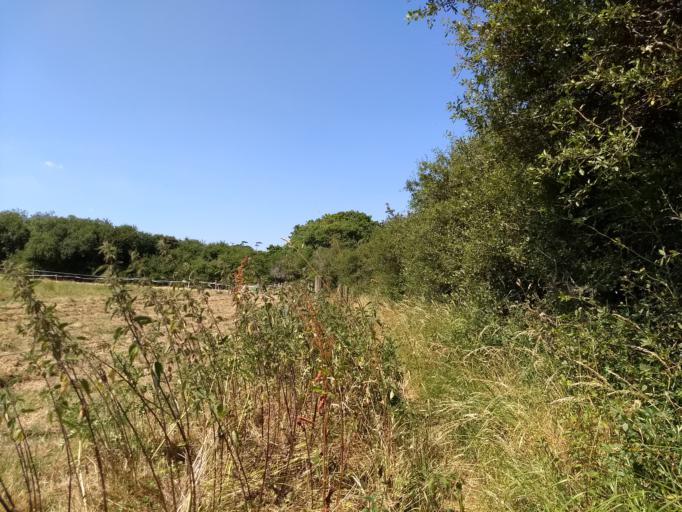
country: GB
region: England
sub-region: Isle of Wight
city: Gurnard
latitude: 50.7284
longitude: -1.3612
